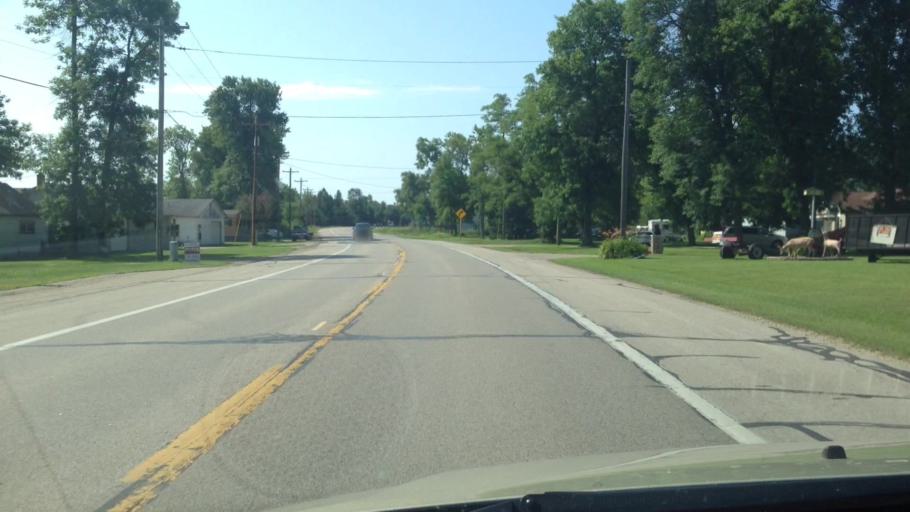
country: US
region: Michigan
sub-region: Delta County
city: Escanaba
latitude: 45.6974
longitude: -87.1015
